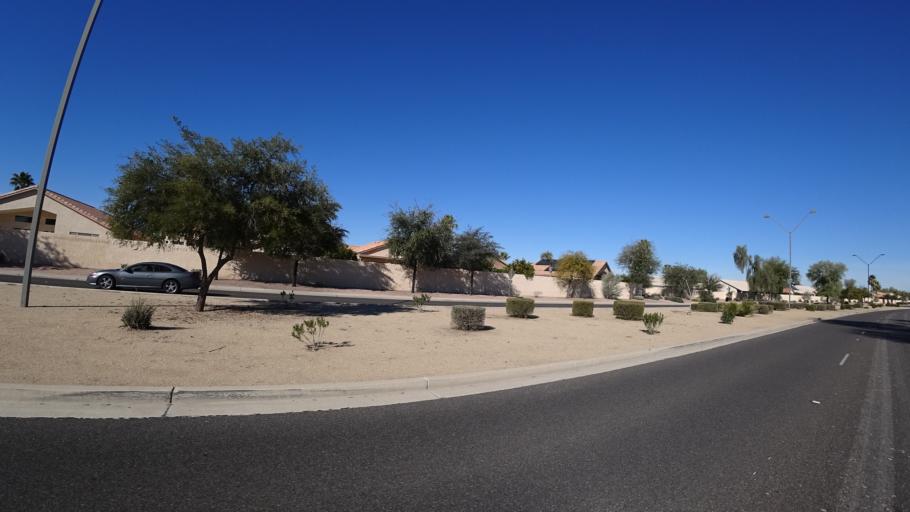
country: US
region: Arizona
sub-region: Maricopa County
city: Litchfield Park
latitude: 33.4798
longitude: -112.3752
